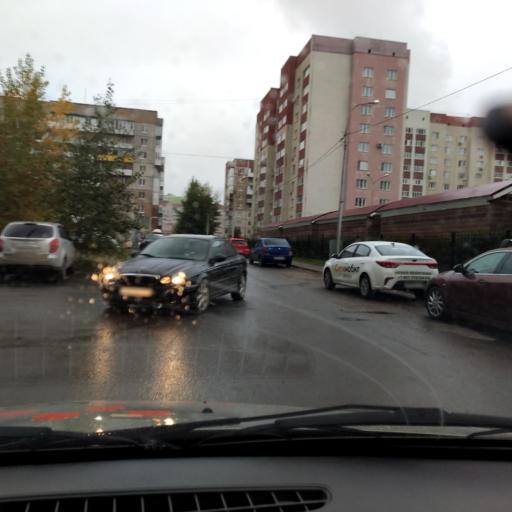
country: RU
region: Bashkortostan
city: Ufa
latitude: 54.7809
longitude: 56.1099
